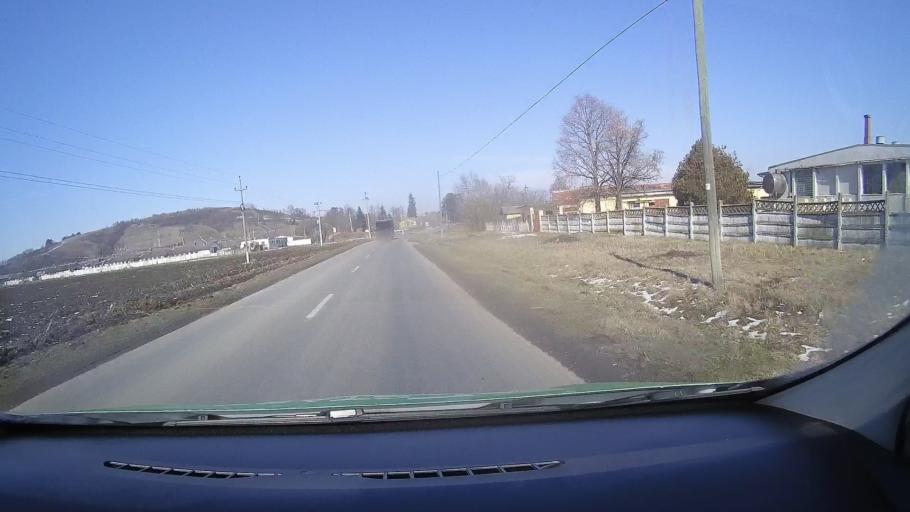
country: RO
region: Brasov
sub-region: Comuna Homorod
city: Homorod
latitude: 46.0341
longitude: 25.2736
